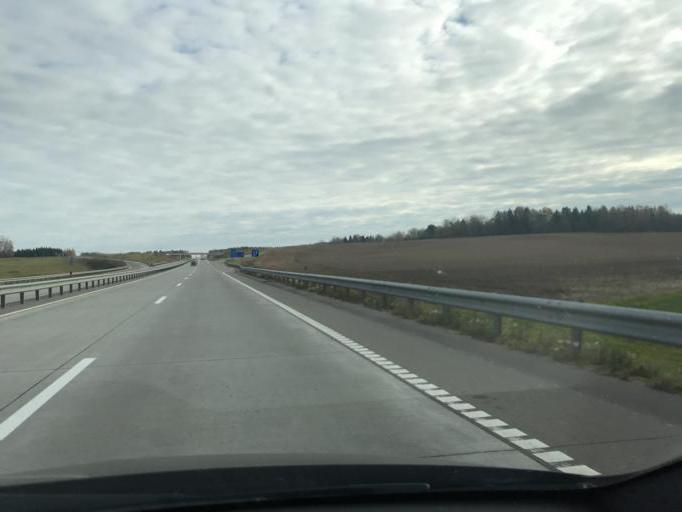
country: BY
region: Minsk
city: Zaslawye
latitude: 54.0637
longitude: 27.3426
